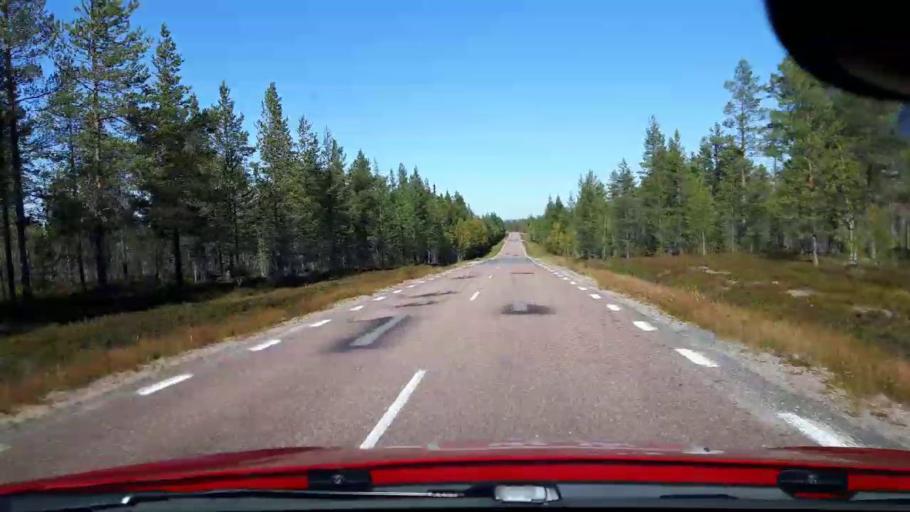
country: SE
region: Jaemtland
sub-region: Harjedalens Kommun
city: Sveg
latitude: 61.7334
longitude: 14.1642
